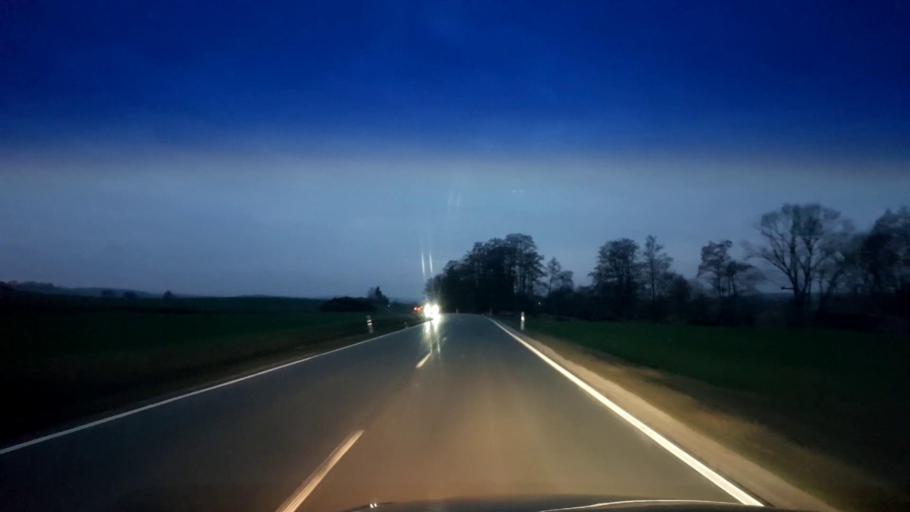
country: DE
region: Bavaria
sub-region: Upper Franconia
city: Burgebrach
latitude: 49.8263
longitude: 10.7204
